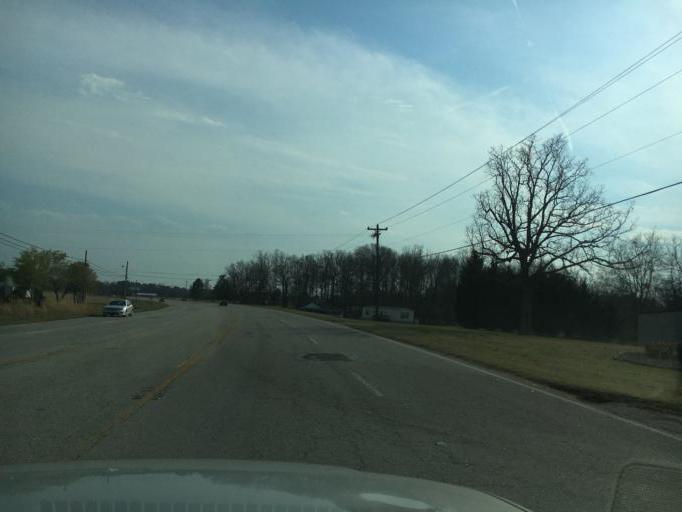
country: US
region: South Carolina
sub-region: Spartanburg County
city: Mayo
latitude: 35.1108
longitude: -81.8563
